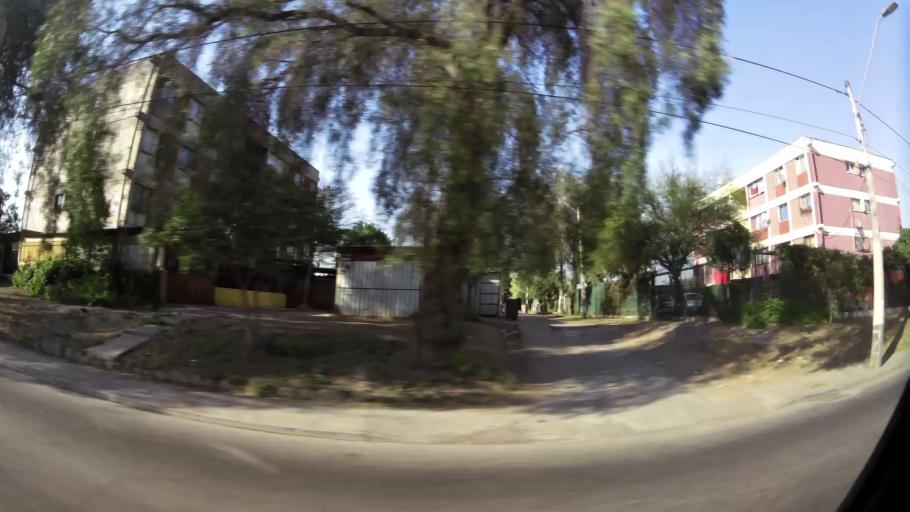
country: CL
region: Santiago Metropolitan
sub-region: Provincia de Santiago
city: Lo Prado
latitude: -33.4134
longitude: -70.7506
